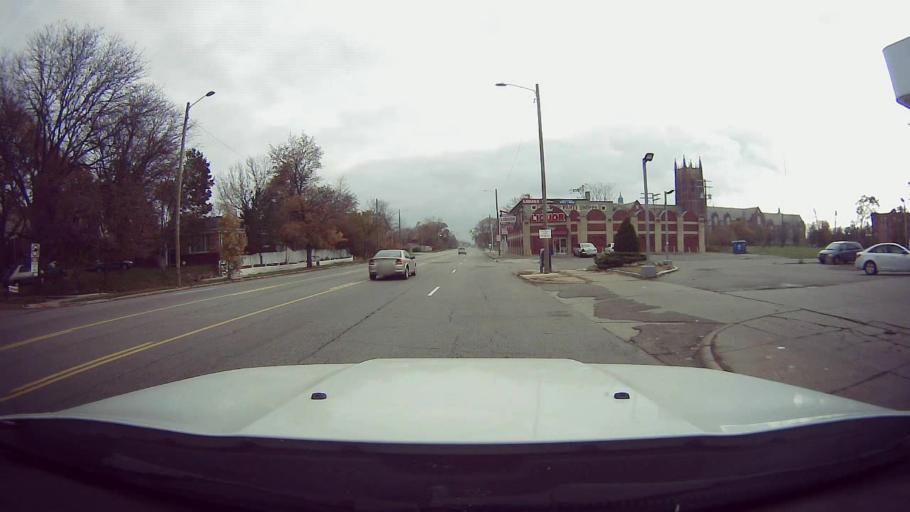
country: US
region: Michigan
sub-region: Wayne County
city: Highland Park
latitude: 42.3776
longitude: -83.1116
